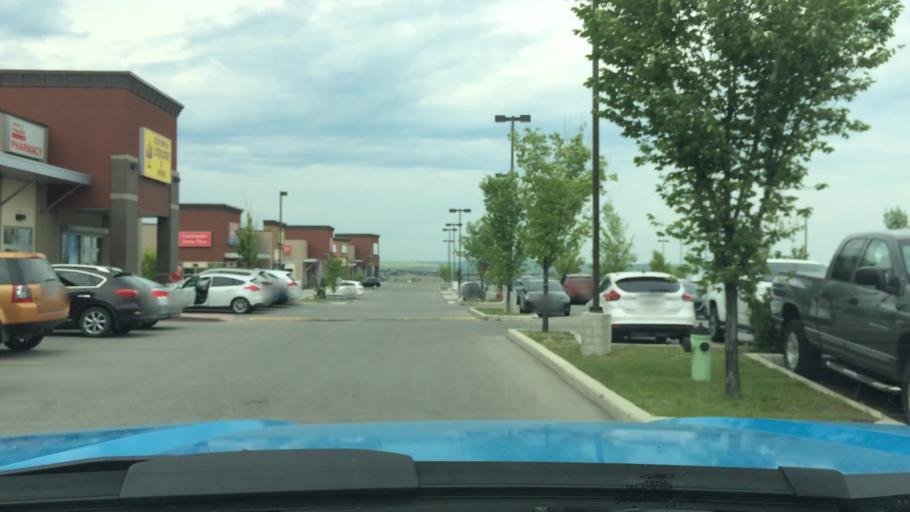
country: CA
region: Alberta
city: Calgary
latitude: 51.1609
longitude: -114.1616
